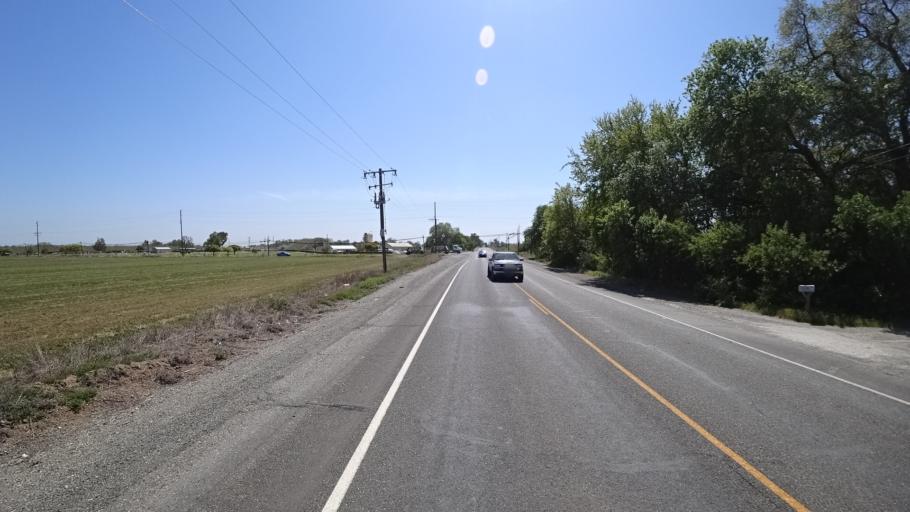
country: US
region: California
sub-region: Glenn County
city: Orland
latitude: 39.7701
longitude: -122.1967
